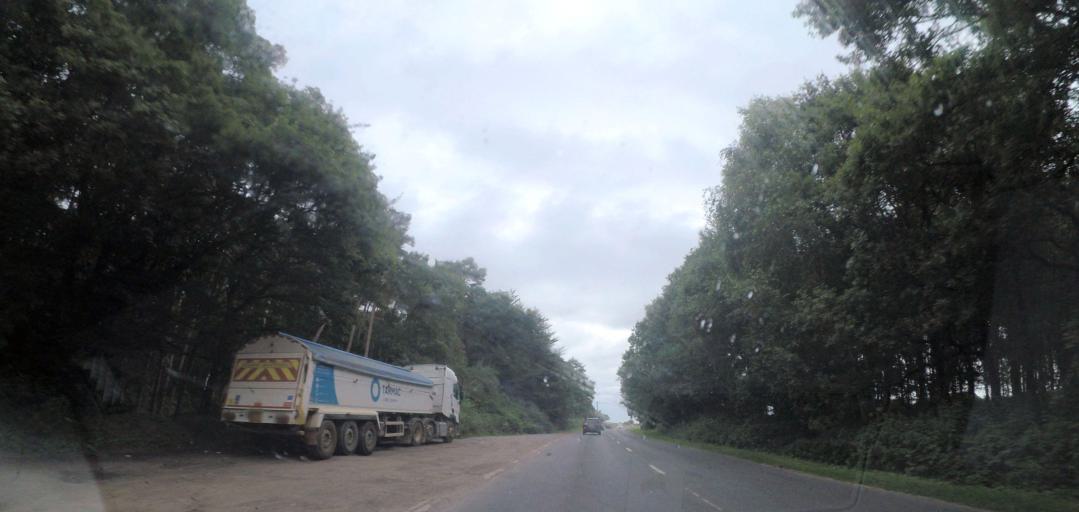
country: GB
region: England
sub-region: Norfolk
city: Spixworth
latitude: 52.7036
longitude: 1.3446
